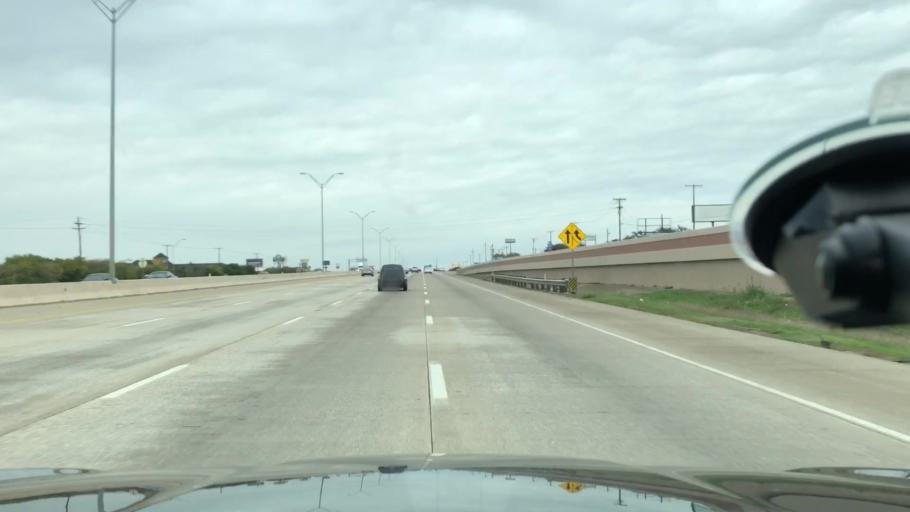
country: US
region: Texas
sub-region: Dallas County
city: DeSoto
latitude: 32.6133
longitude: -96.8229
